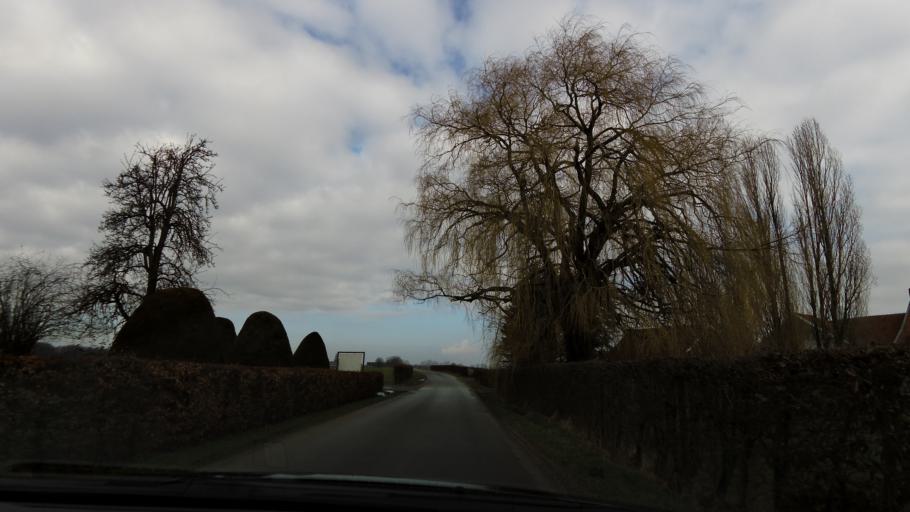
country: BE
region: Flanders
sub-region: Provincie Limburg
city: Sint-Pieters-Voeren
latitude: 50.7646
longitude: 5.8848
